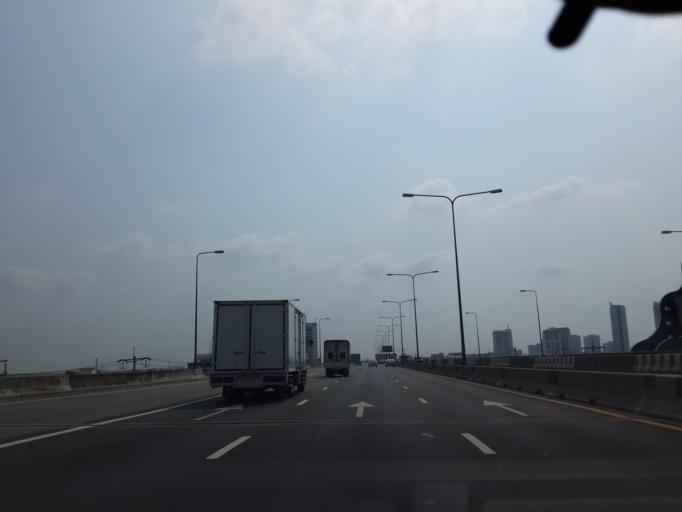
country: TH
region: Bangkok
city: Bang Na
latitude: 13.6647
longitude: 100.6505
